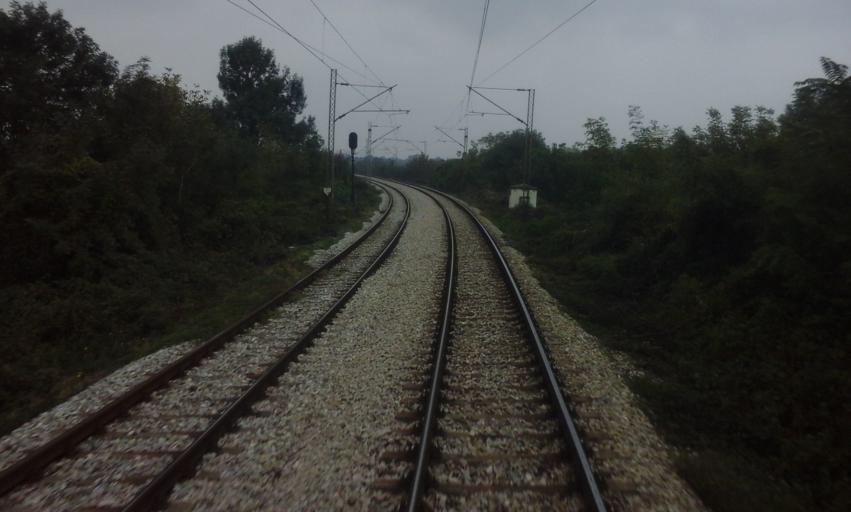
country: RS
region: Central Serbia
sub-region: Sumadijski Okrug
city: Lapovo
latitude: 44.2078
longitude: 21.0929
